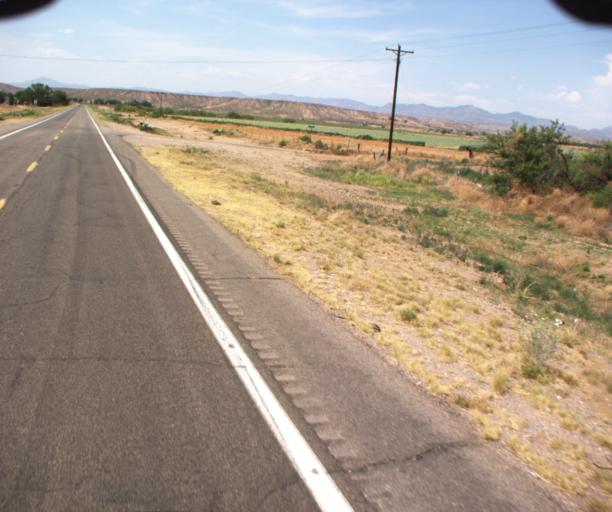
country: US
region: Arizona
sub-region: Greenlee County
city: Clifton
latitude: 32.8456
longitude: -109.1813
